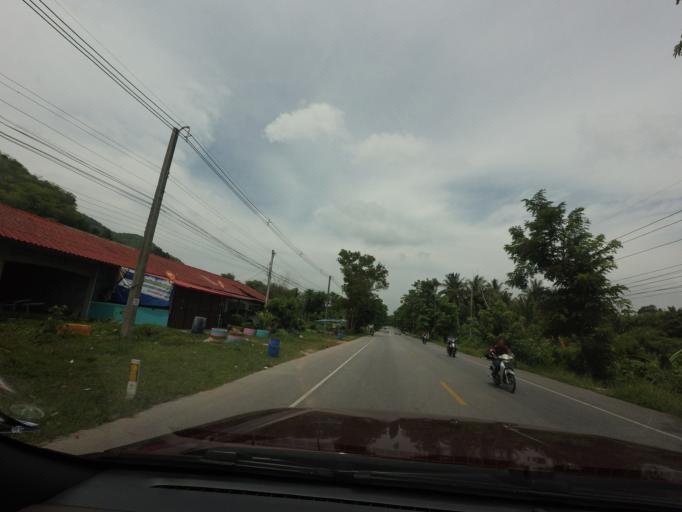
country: TH
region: Pattani
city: Mae Lan
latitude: 6.6317
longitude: 101.3022
